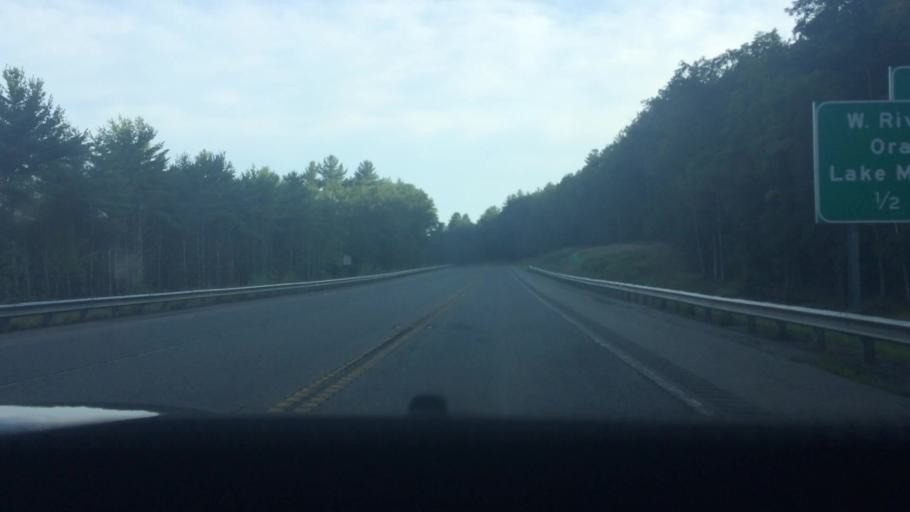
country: US
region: Massachusetts
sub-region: Franklin County
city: Orange
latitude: 42.5816
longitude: -72.3254
